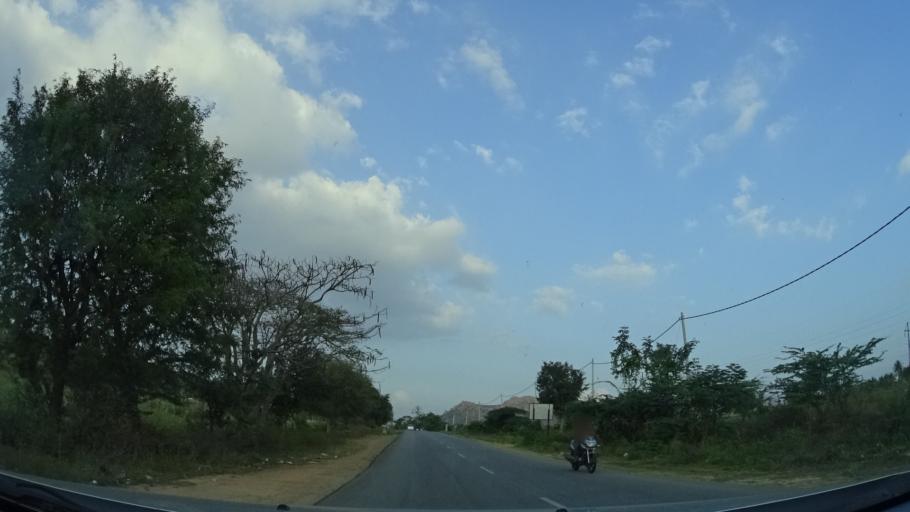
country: IN
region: Karnataka
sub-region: Ramanagara
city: Kanakapura
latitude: 12.4560
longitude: 77.3243
